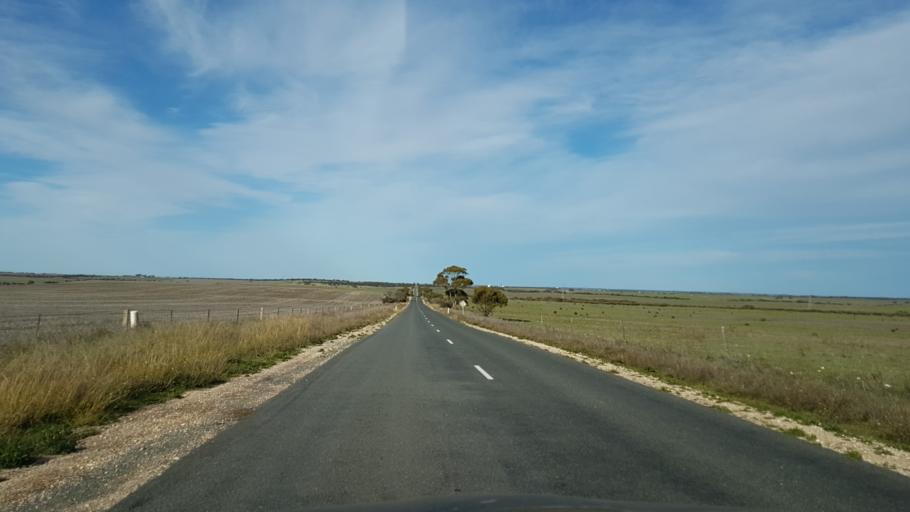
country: AU
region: South Australia
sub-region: Murray Bridge
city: Tailem Bend
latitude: -35.1837
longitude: 139.4552
